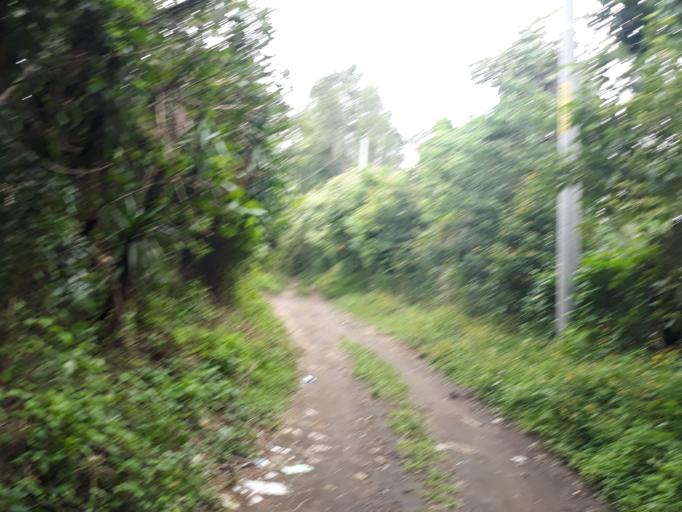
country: GT
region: Escuintla
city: San Vicente Pacaya
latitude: 14.3672
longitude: -90.5536
